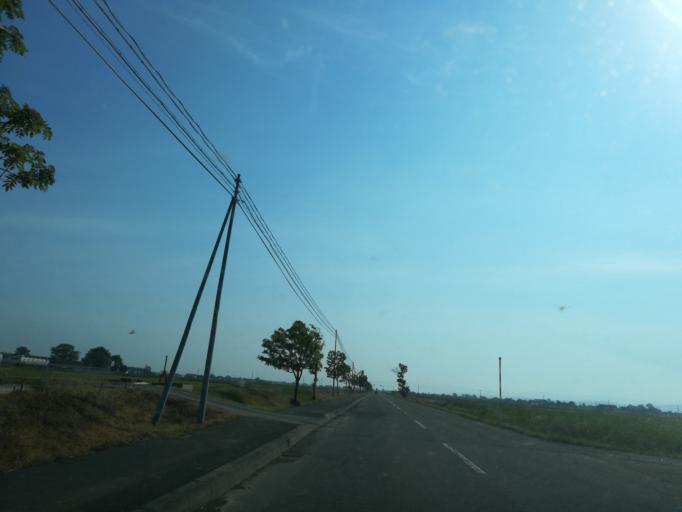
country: JP
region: Hokkaido
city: Iwamizawa
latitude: 43.1565
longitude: 141.6782
